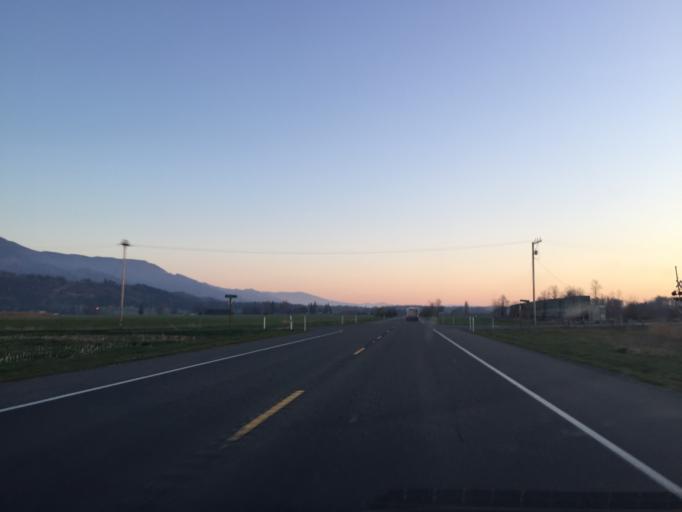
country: US
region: Washington
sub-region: Whatcom County
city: Sumas
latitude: 48.9756
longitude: -122.2712
